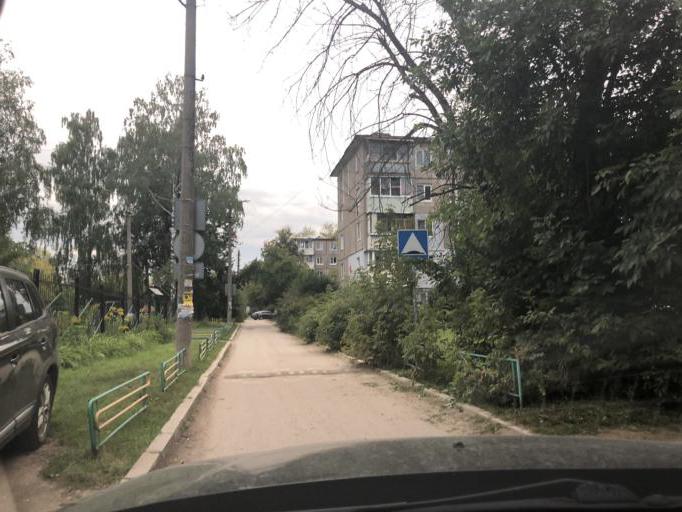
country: RU
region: Tula
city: Tula
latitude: 54.1946
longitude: 37.6725
